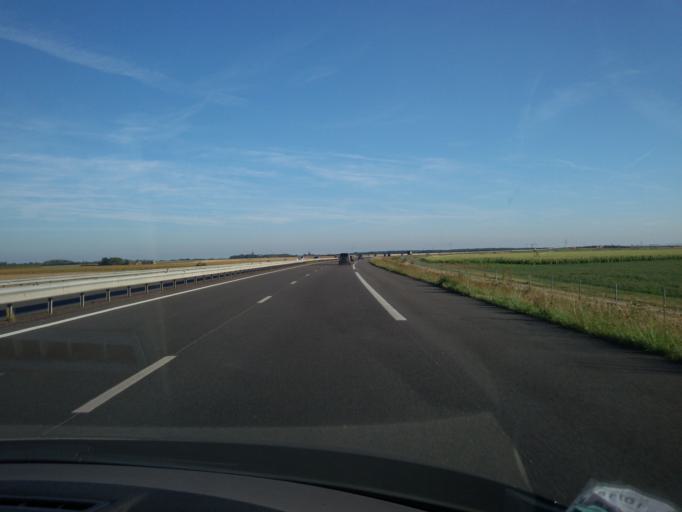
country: FR
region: Centre
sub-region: Departement du Cher
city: Levet
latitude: 46.9442
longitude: 2.4170
